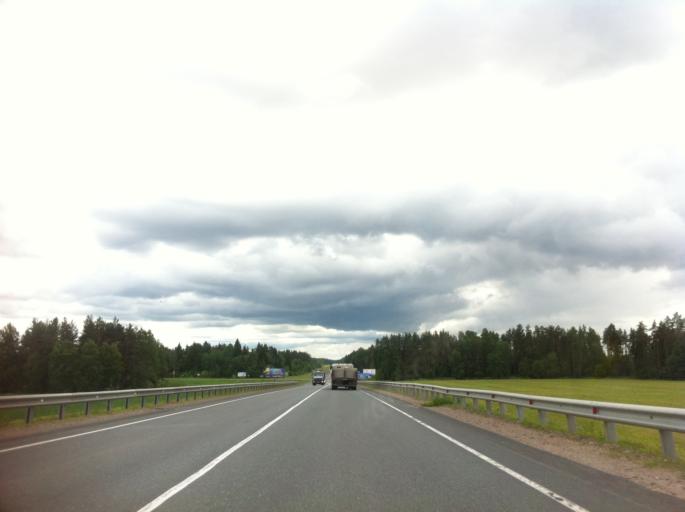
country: RU
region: Leningrad
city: Luga
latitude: 58.6933
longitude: 29.8776
